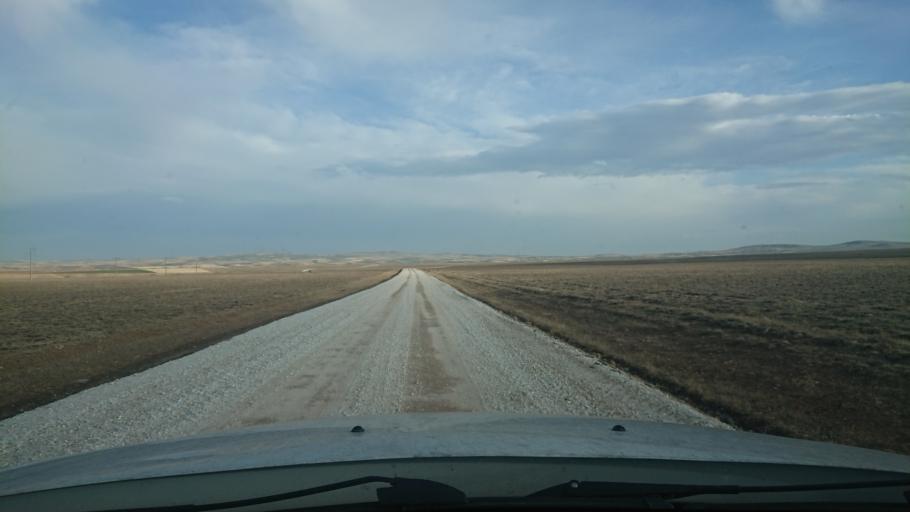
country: TR
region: Aksaray
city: Agacoren
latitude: 38.7250
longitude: 33.8675
